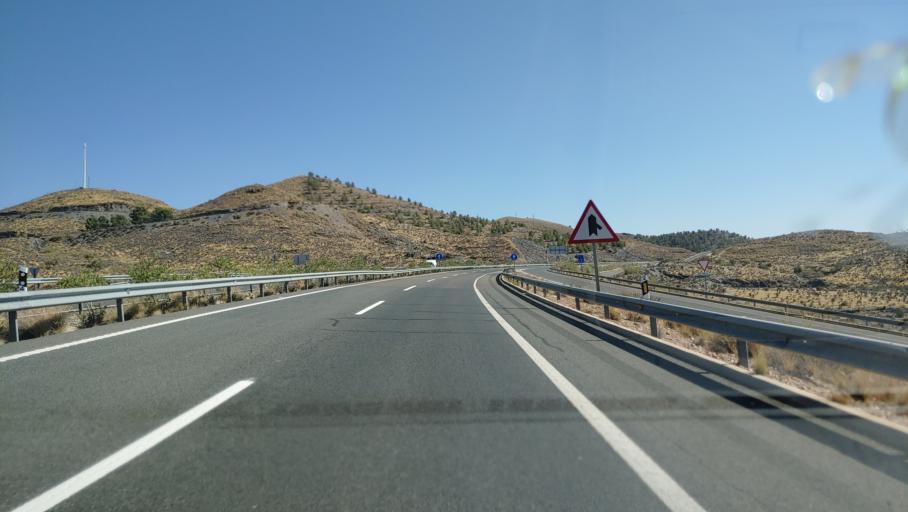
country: ES
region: Andalusia
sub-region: Provincia de Almeria
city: Gergal
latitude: 37.1100
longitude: -2.5288
